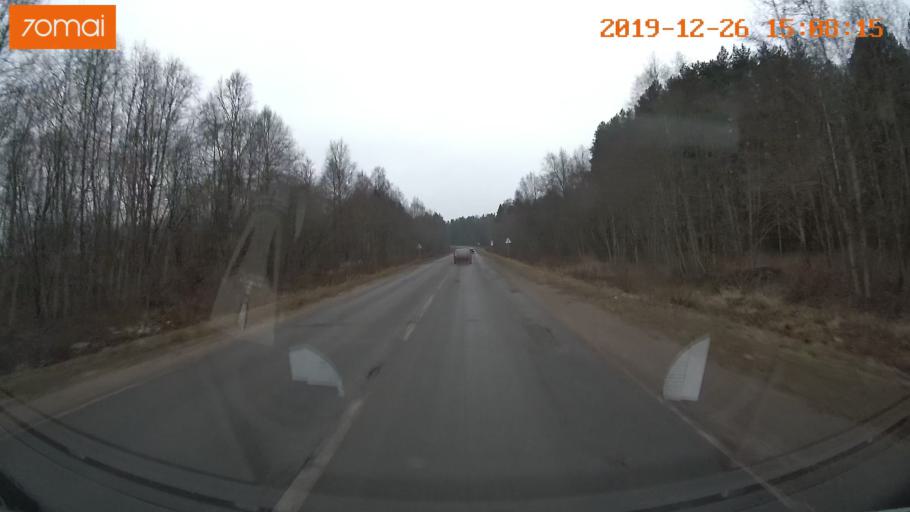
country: RU
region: Jaroslavl
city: Rybinsk
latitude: 58.1617
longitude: 38.8393
